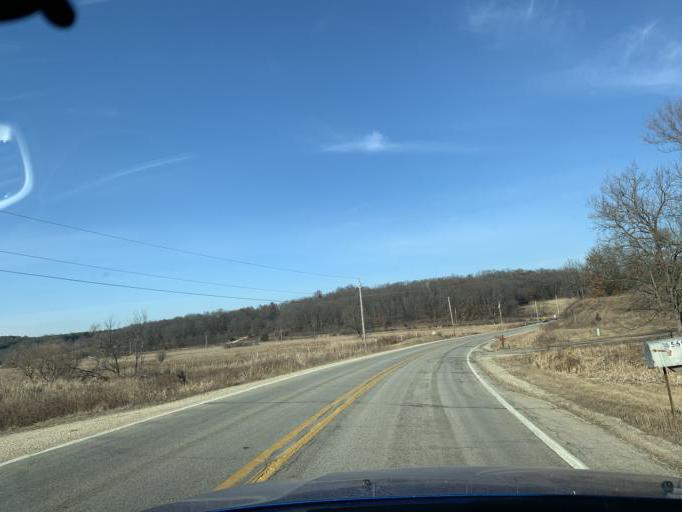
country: US
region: Wisconsin
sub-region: Green County
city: New Glarus
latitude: 42.7359
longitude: -89.8609
